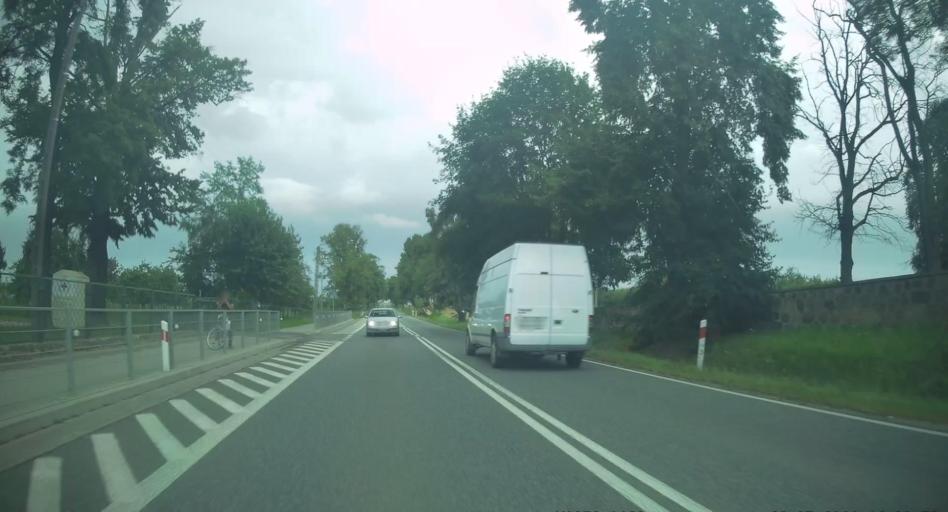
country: PL
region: Lodz Voivodeship
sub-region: Powiat skierniewicki
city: Gluchow
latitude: 51.7789
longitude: 20.0827
